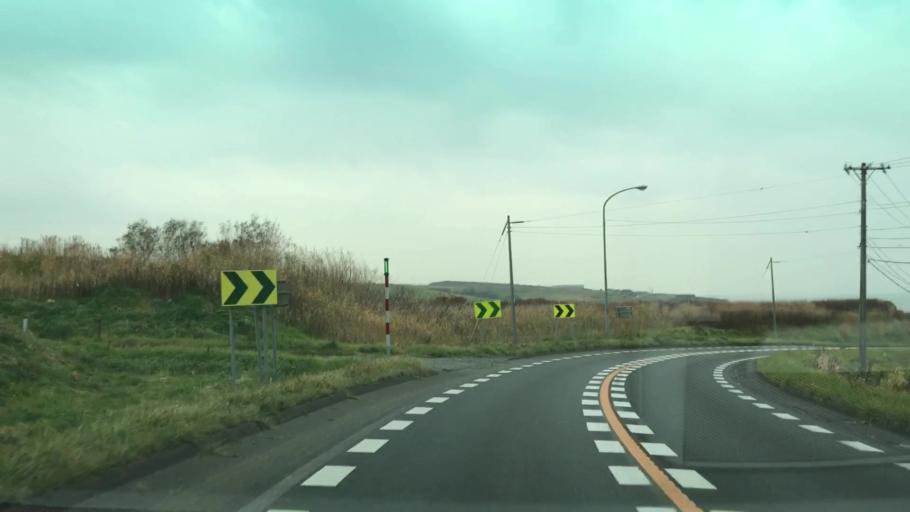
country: JP
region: Hokkaido
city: Ishikari
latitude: 43.3614
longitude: 141.4309
